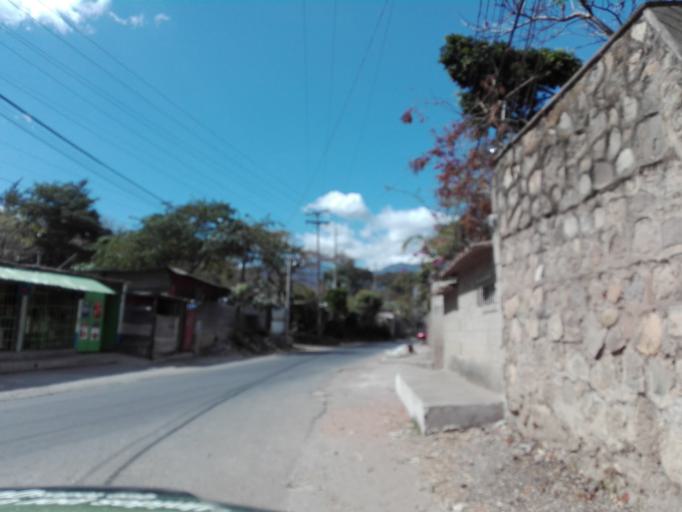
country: GT
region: Guatemala
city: Amatitlan
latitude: 14.4720
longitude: -90.6061
